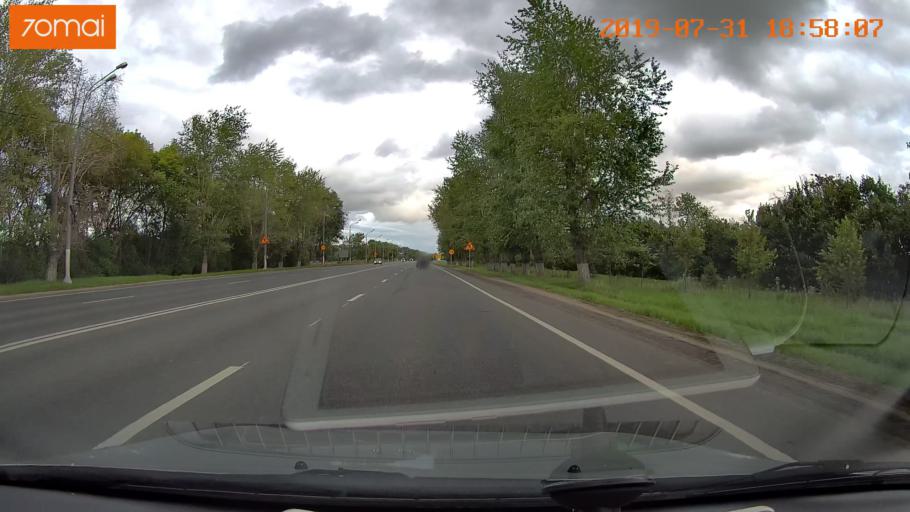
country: RU
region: Moskovskaya
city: Raduzhnyy
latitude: 55.1490
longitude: 38.7006
